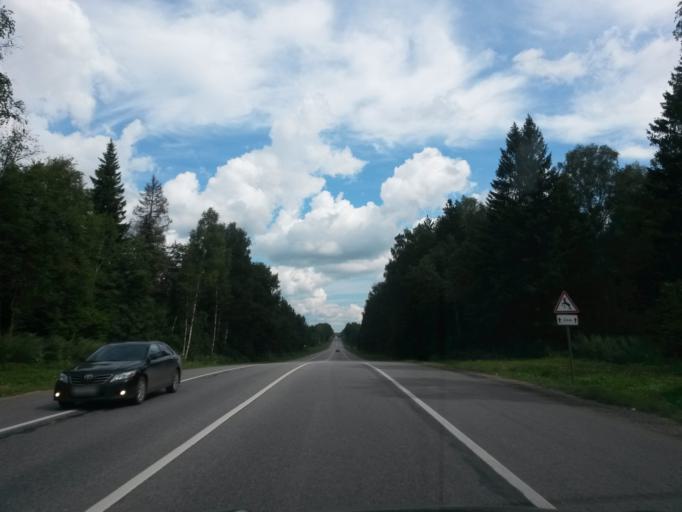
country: RU
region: Jaroslavl
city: Pereslavl'-Zalesskiy
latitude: 56.6371
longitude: 38.6783
